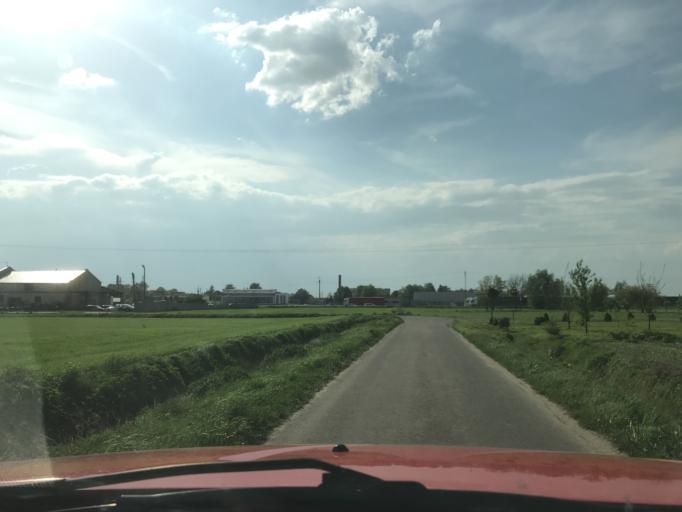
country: PL
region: Greater Poland Voivodeship
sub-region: Powiat kaliski
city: Stawiszyn
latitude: 51.9207
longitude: 18.1220
